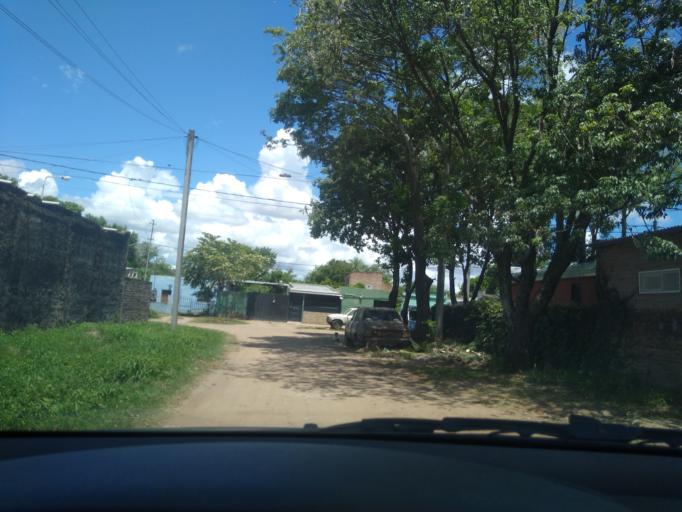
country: AR
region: Chaco
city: Barranqueras
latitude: -27.4768
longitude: -58.9350
